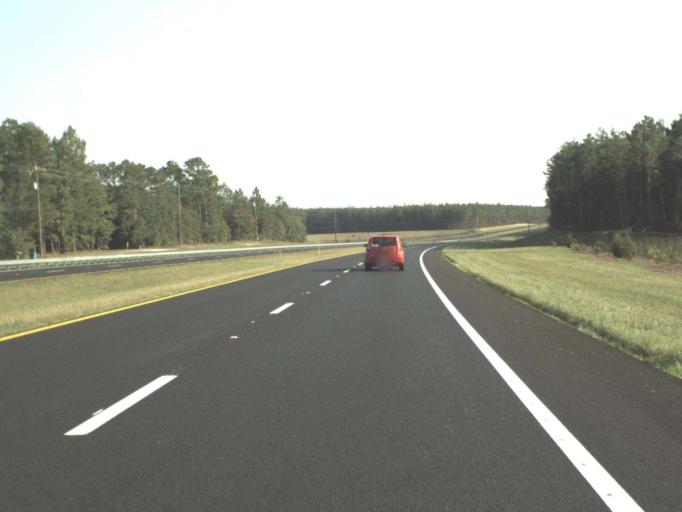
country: US
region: Florida
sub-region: Holmes County
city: Bonifay
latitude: 30.5400
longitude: -85.8334
